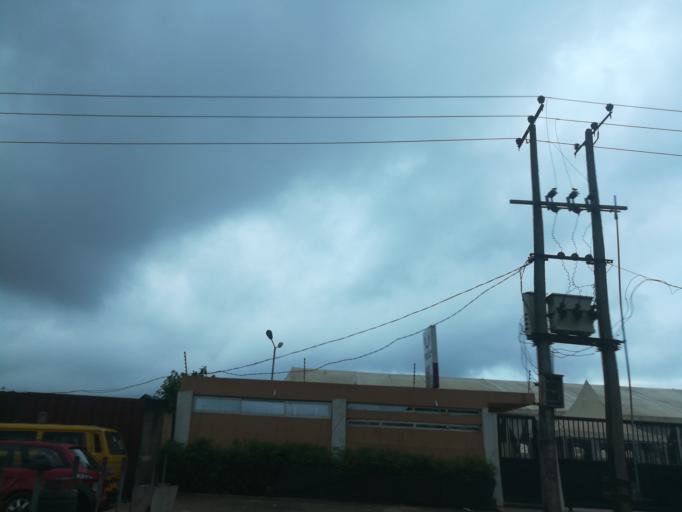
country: NG
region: Lagos
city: Agege
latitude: 6.6118
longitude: 3.3289
